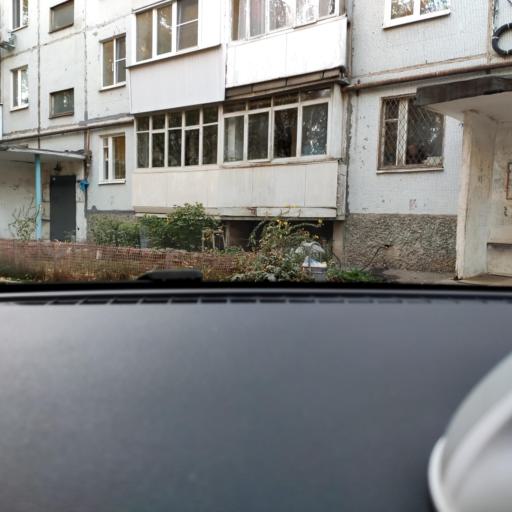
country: RU
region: Samara
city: Petra-Dubrava
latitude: 53.2477
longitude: 50.3123
